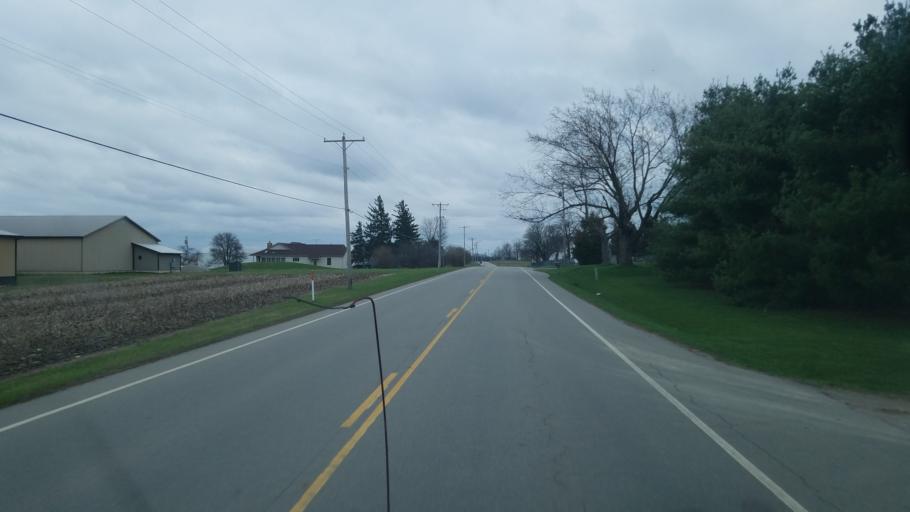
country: US
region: Ohio
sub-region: Fayette County
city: Washington Court House
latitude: 39.5569
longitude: -83.4931
